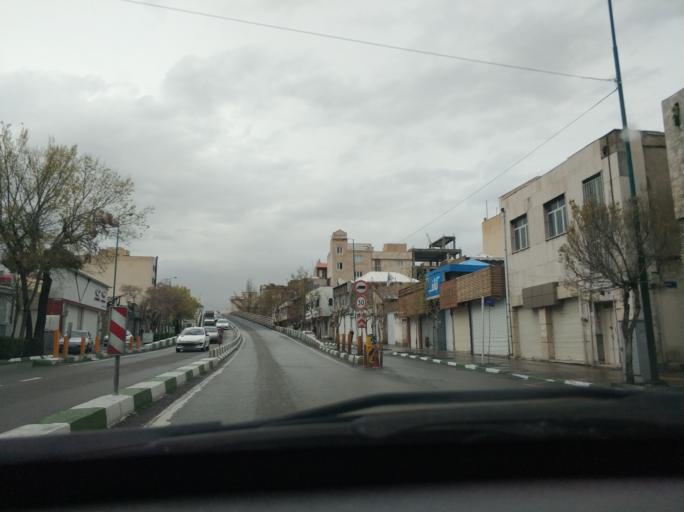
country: IR
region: Tehran
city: Tehran
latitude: 35.7002
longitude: 51.4378
